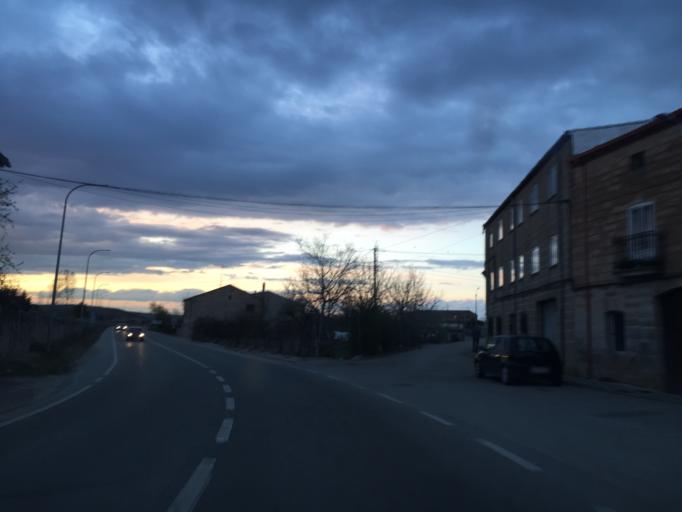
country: ES
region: Castille and Leon
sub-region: Provincia de Burgos
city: Tardajos
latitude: 42.3499
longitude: -3.8158
